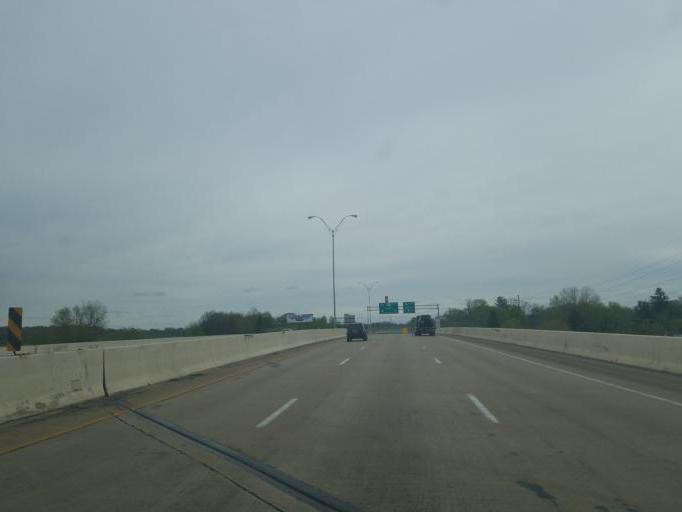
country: US
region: Ohio
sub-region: Summit County
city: Barberton
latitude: 41.0355
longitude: -81.5764
